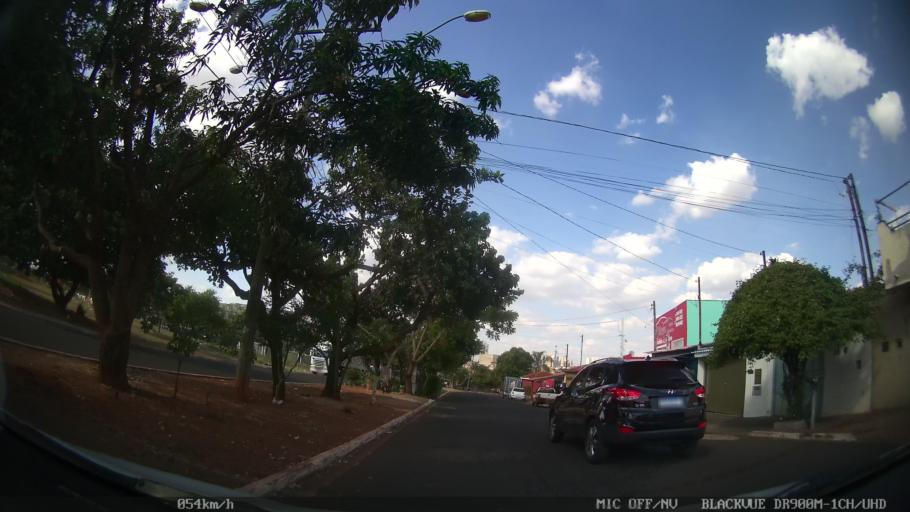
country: BR
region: Sao Paulo
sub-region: Ribeirao Preto
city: Ribeirao Preto
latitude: -21.1974
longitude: -47.8326
